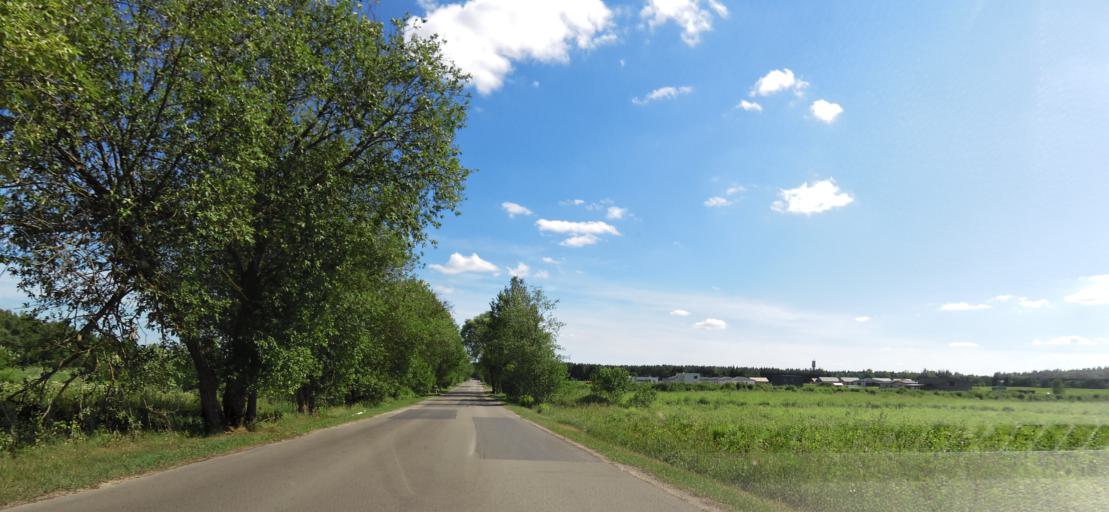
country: LT
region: Vilnius County
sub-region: Vilnius
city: Fabijoniskes
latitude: 54.8104
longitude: 25.3243
